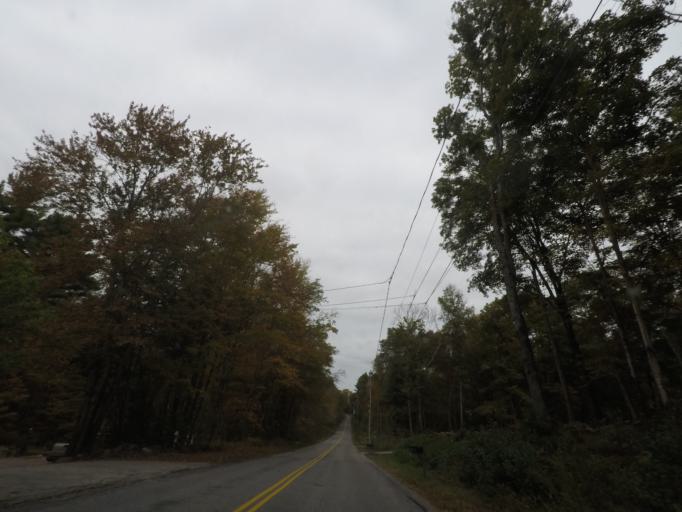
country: US
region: Connecticut
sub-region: Windham County
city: Thompson
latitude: 41.9449
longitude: -71.8346
